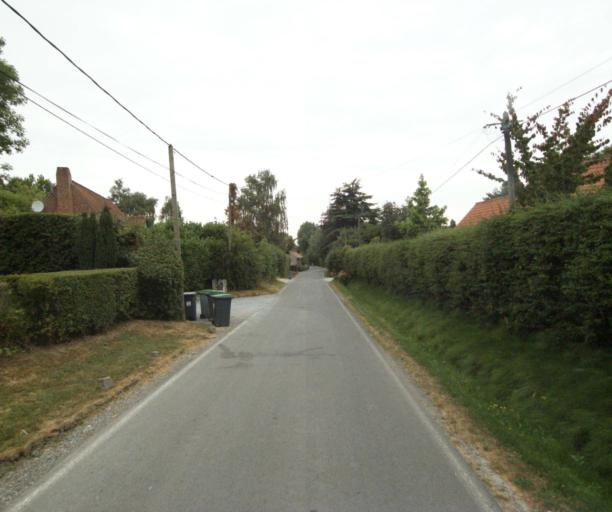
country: FR
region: Nord-Pas-de-Calais
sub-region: Departement du Nord
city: Bondues
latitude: 50.7221
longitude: 3.1010
